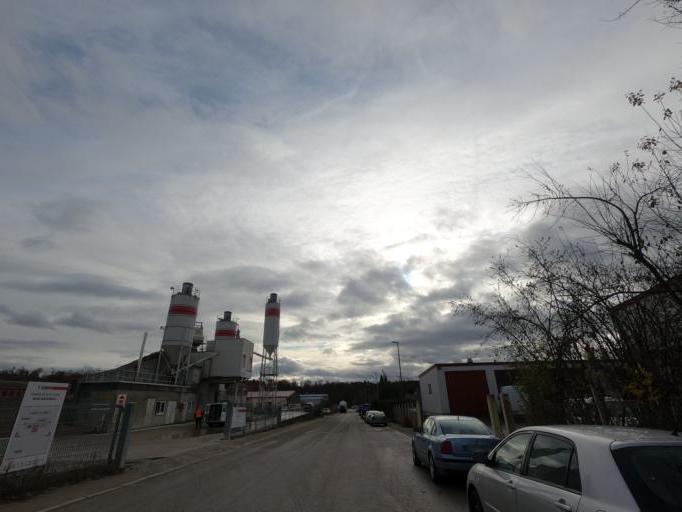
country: DE
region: Baden-Wuerttemberg
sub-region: Regierungsbezirk Stuttgart
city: Schlierbach
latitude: 48.6734
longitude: 9.5308
